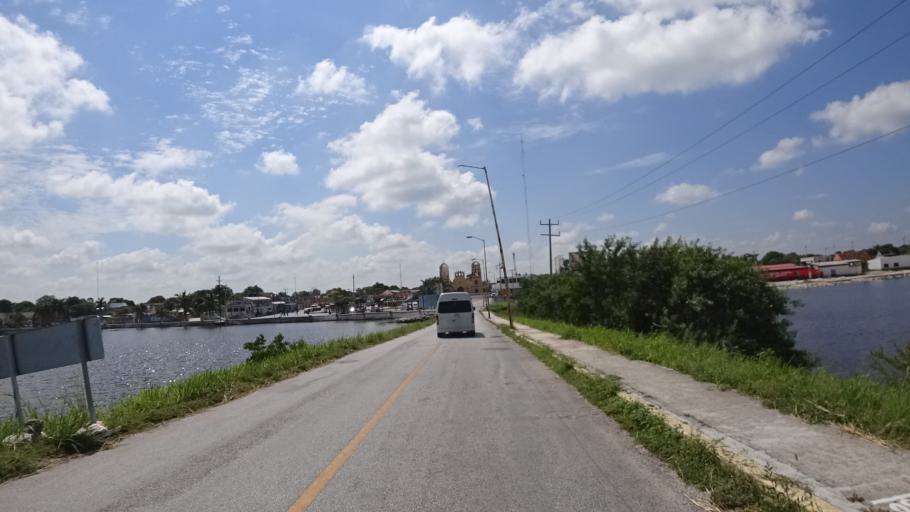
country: MX
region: Campeche
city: Sabancuy
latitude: 18.9761
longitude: -91.1811
